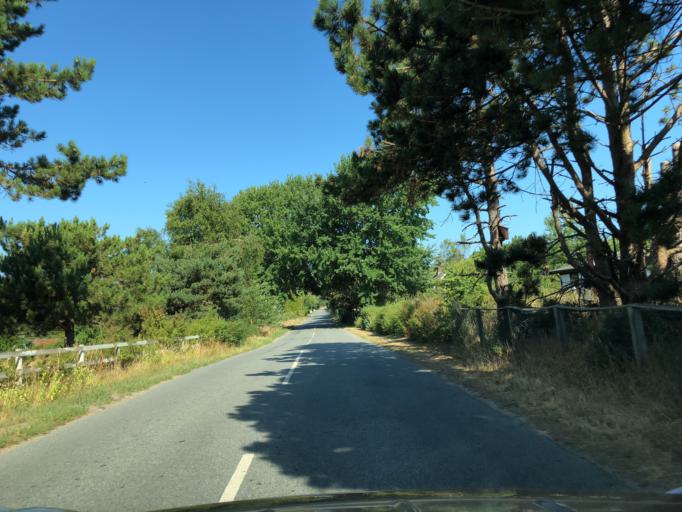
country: DK
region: Zealand
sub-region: Odsherred Kommune
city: Asnaes
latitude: 55.9847
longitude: 11.3032
